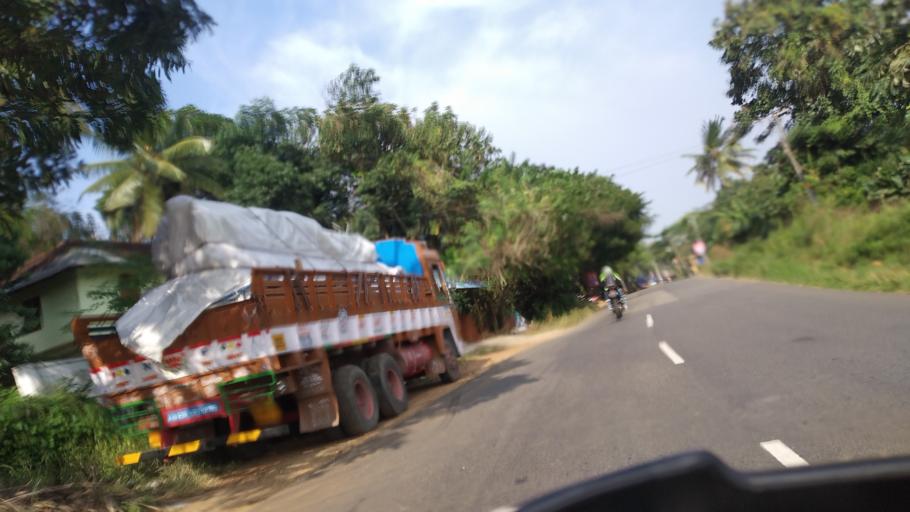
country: IN
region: Kerala
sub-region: Palakkad district
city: Palakkad
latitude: 10.6006
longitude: 76.5362
